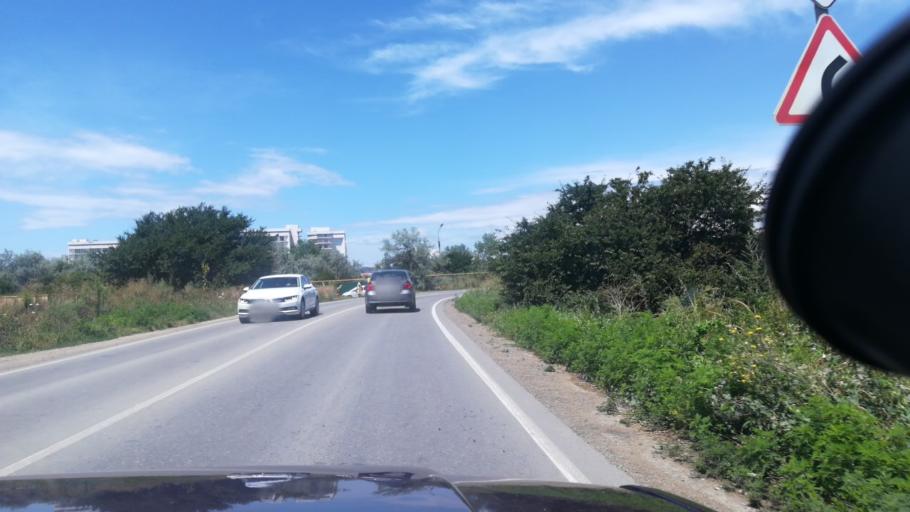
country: RU
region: Krasnodarskiy
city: Vityazevo
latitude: 44.9634
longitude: 37.2915
